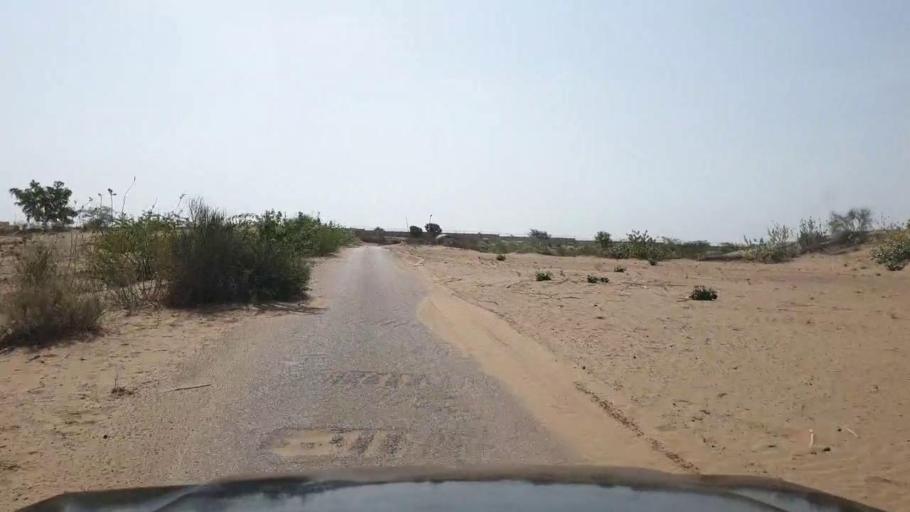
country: PK
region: Sindh
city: Islamkot
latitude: 24.9201
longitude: 70.1452
